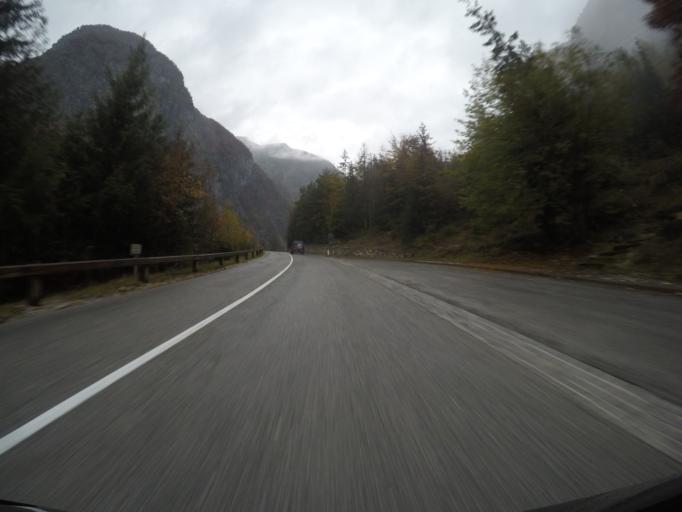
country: SI
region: Kranjska Gora
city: Kranjska Gora
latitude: 46.3852
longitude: 13.7525
